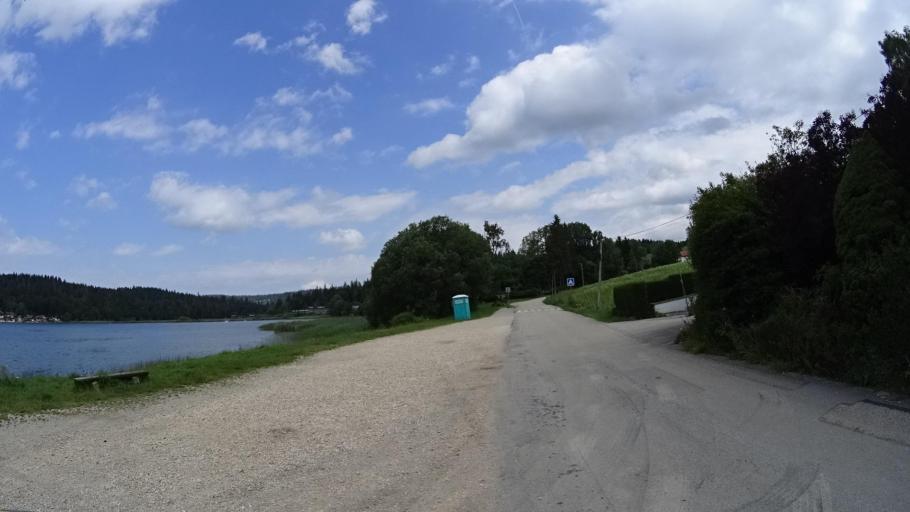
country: FR
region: Franche-Comte
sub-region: Departement du Doubs
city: Les Fourgs
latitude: 46.8341
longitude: 6.3401
